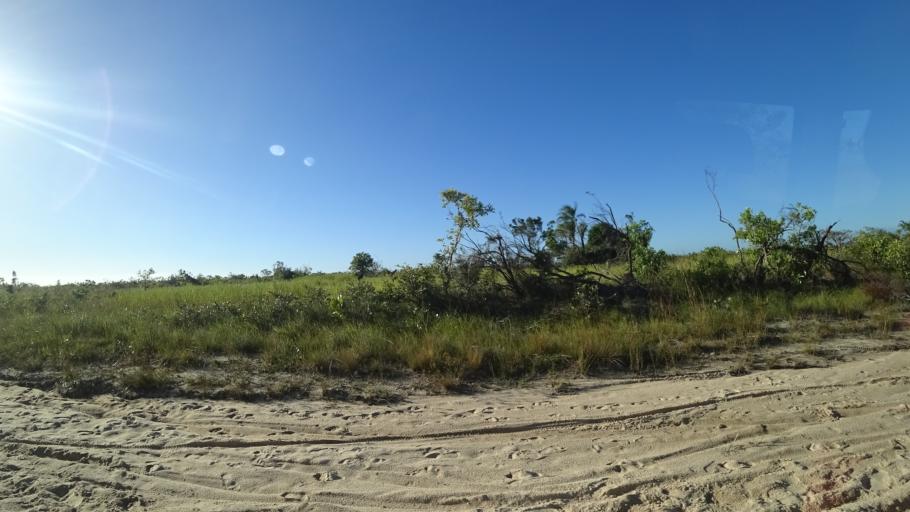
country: MZ
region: Sofala
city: Beira
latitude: -19.5738
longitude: 35.2442
